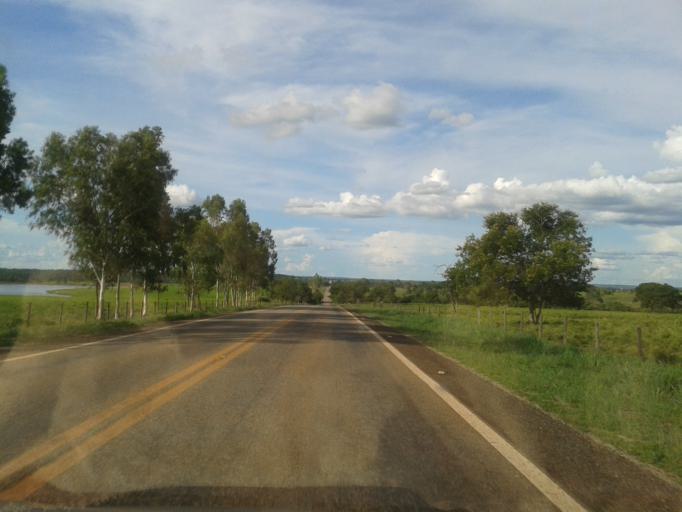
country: BR
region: Goias
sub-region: Crixas
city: Crixas
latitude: -14.2460
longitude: -50.3962
